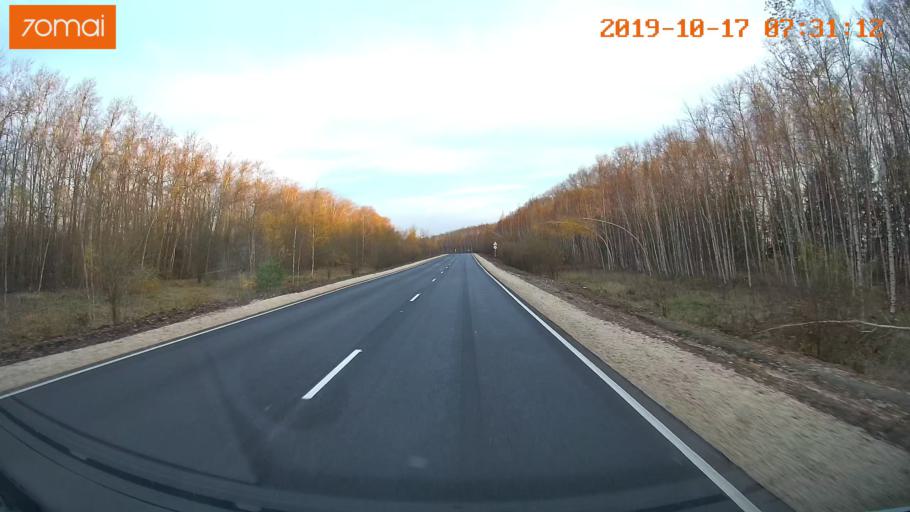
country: RU
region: Ivanovo
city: Gavrilov Posad
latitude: 56.3861
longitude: 40.0001
